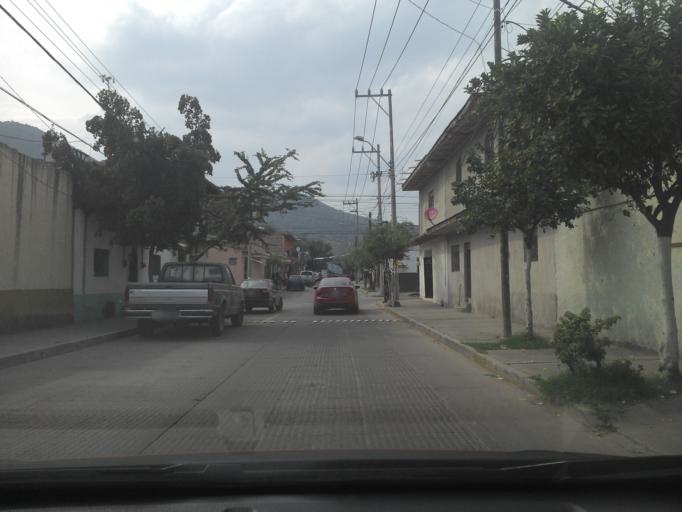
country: MX
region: Jalisco
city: Tlajomulco de Zuniga
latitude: 20.4777
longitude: -103.4480
